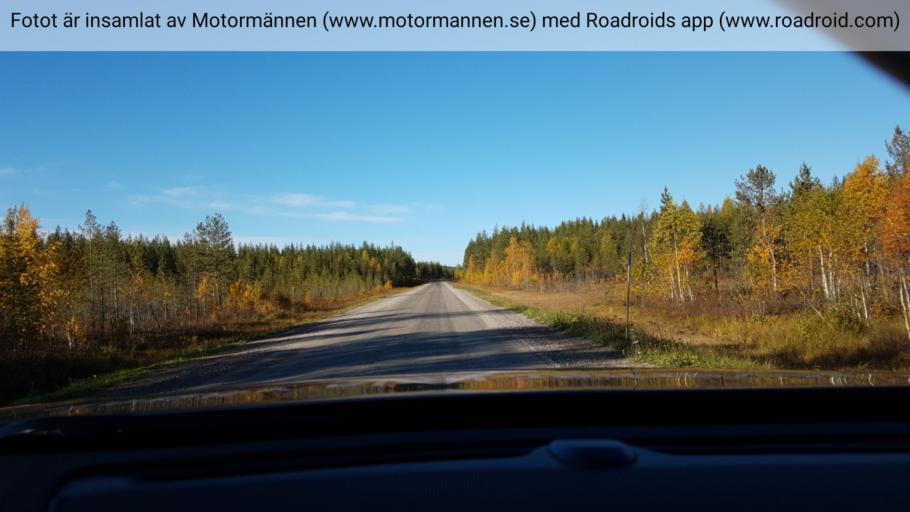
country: SE
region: Norrbotten
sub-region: Alvsbyns Kommun
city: AElvsbyn
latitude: 66.2653
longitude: 21.0537
